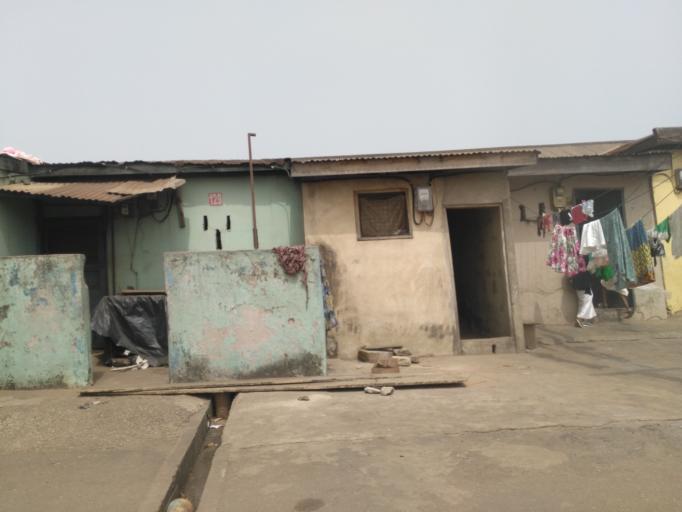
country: GH
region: Ashanti
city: Kumasi
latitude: 6.6975
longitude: -1.6059
